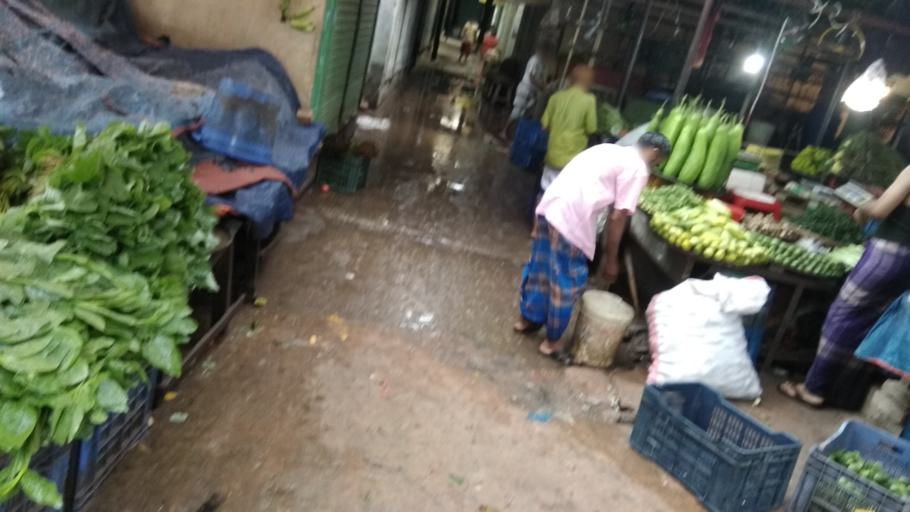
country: BD
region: Dhaka
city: Tungi
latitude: 23.8272
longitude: 90.3697
